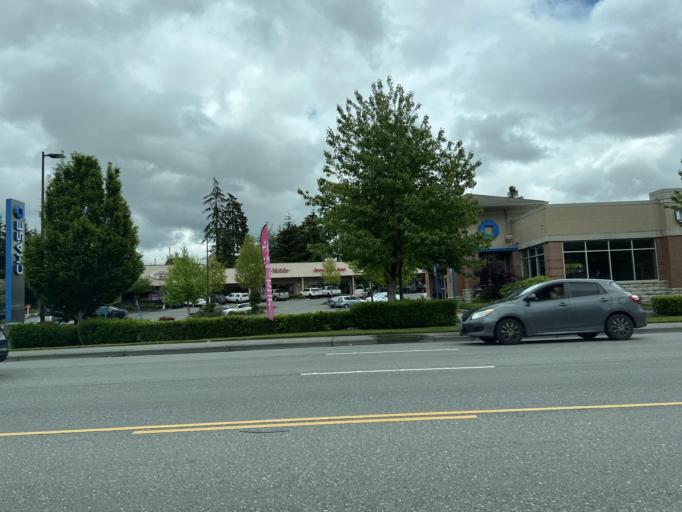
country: US
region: Washington
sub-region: Snohomish County
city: Everett
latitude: 47.9536
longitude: -122.2134
